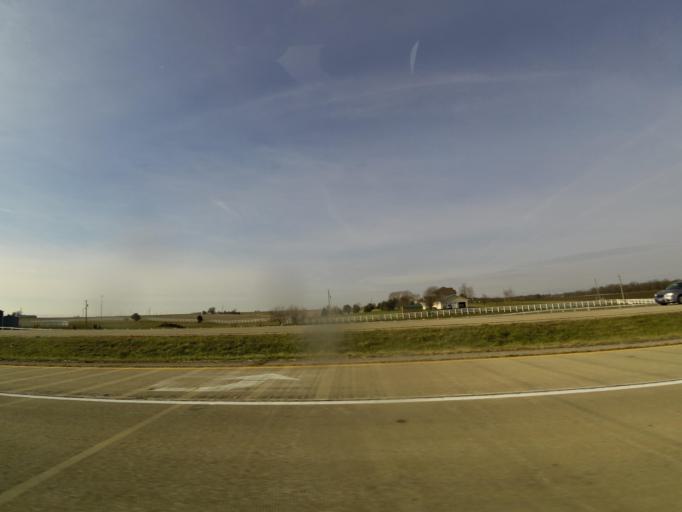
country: US
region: Illinois
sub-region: Macon County
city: Maroa
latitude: 40.0839
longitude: -88.9656
